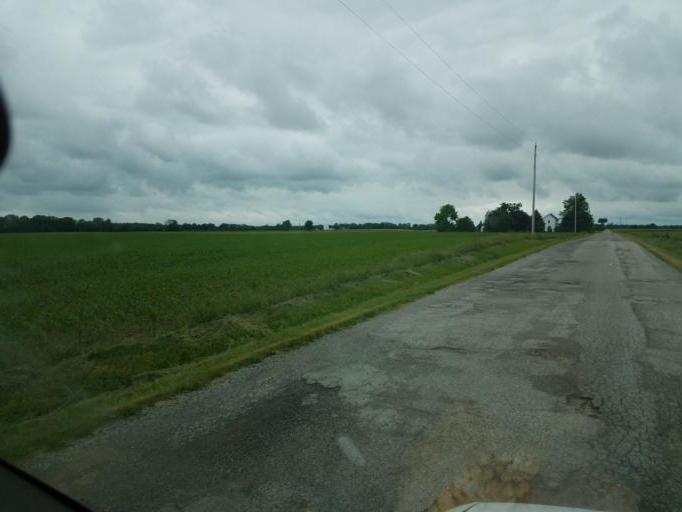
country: US
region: Ohio
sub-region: Morrow County
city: Cardington
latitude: 40.5591
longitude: -82.9003
